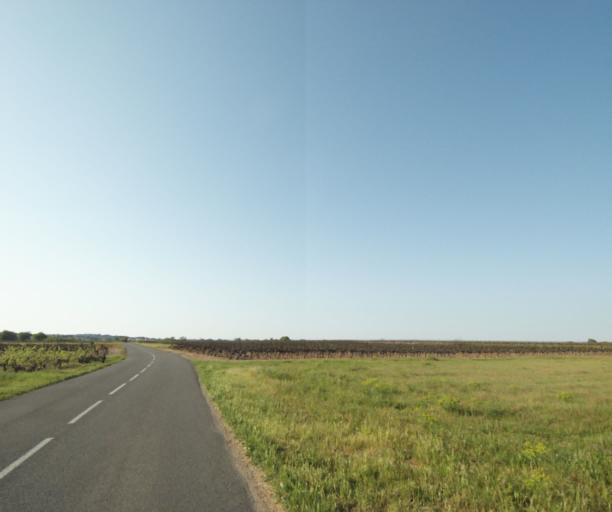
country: FR
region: Languedoc-Roussillon
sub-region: Departement de l'Herault
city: Laverune
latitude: 43.5959
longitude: 3.7946
